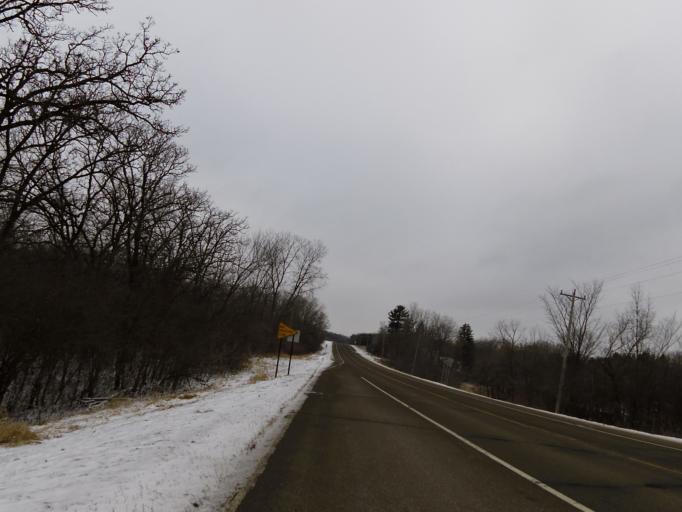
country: US
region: Minnesota
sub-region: Washington County
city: Lakeland
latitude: 44.9634
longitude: -92.8249
